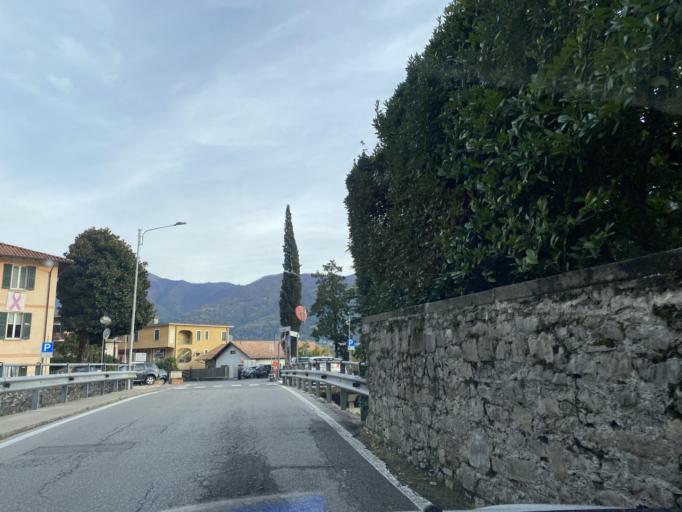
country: IT
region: Lombardy
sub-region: Provincia di Como
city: San Mamete
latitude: 46.0248
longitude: 9.0519
